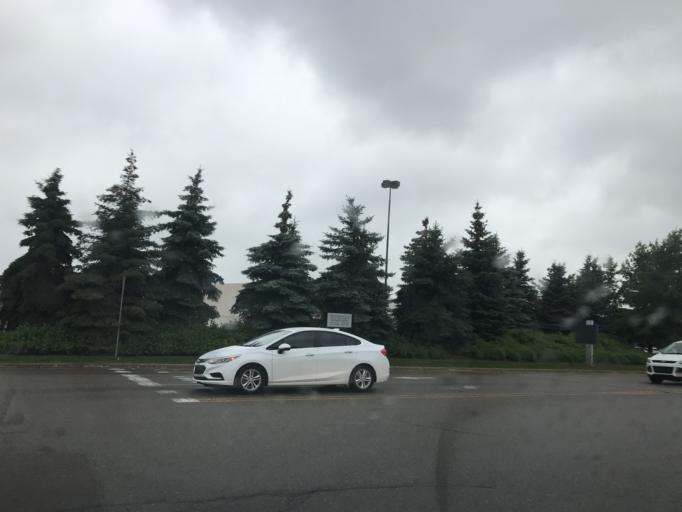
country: US
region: Michigan
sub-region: Oakland County
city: Novi
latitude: 42.4949
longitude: -83.4702
